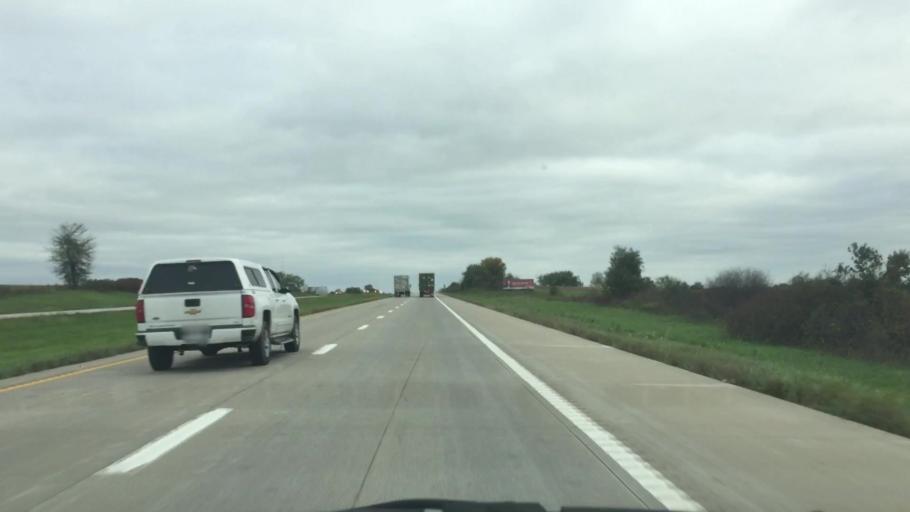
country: US
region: Missouri
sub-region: Clinton County
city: Cameron
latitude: 39.6396
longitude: -94.2427
